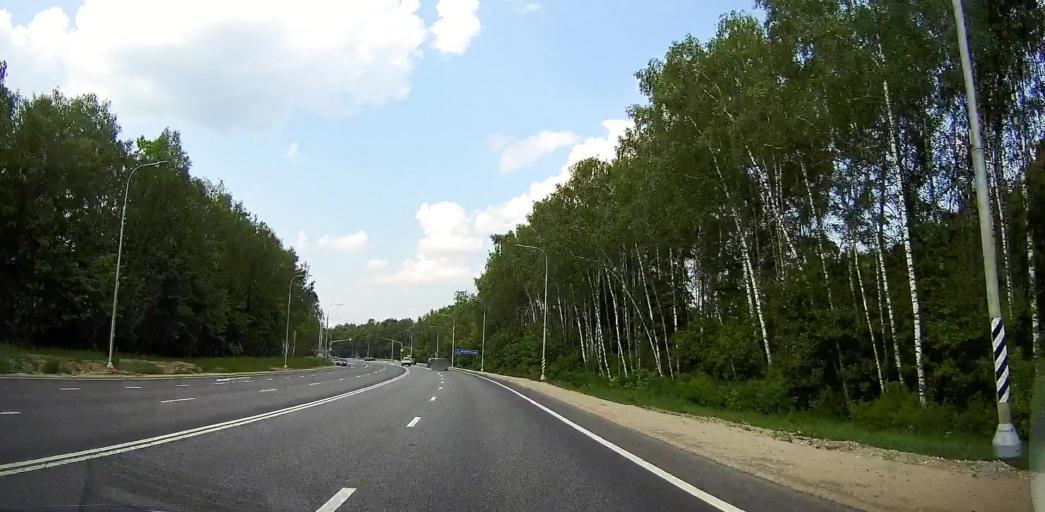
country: RU
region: Moskovskaya
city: Mikhnevo
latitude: 55.0875
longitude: 37.9553
